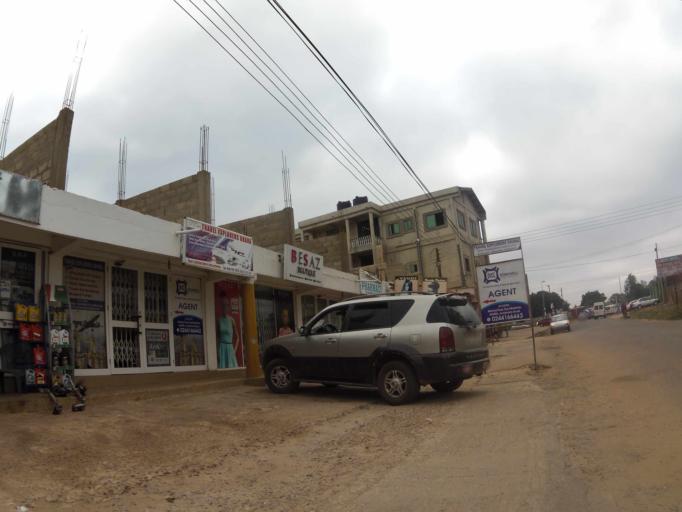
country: GH
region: Greater Accra
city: Dome
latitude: 5.6391
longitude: -0.2112
